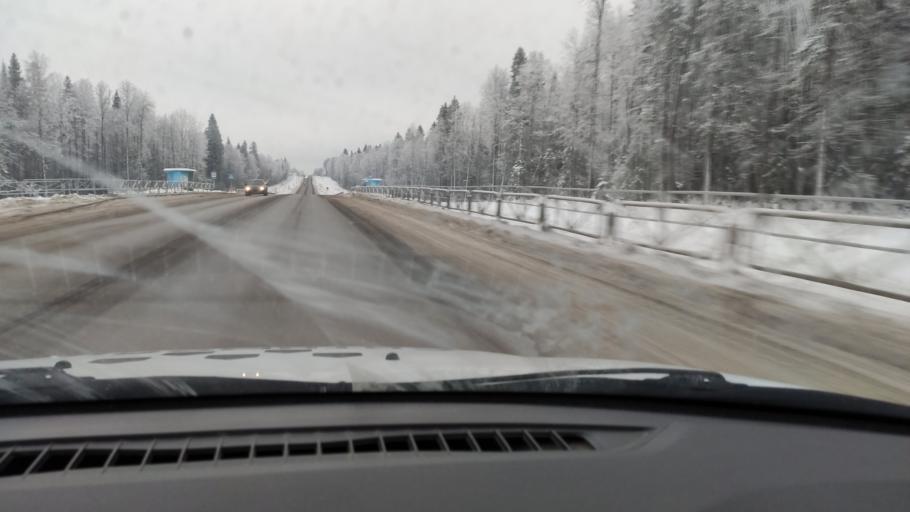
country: RU
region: Perm
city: Novyye Lyady
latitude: 58.0491
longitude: 56.5595
